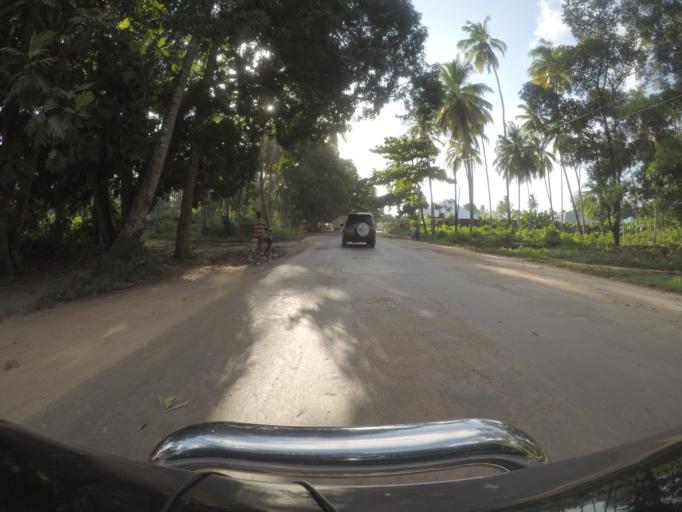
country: TZ
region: Zanzibar Central/South
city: Koani
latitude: -6.1948
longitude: 39.2865
